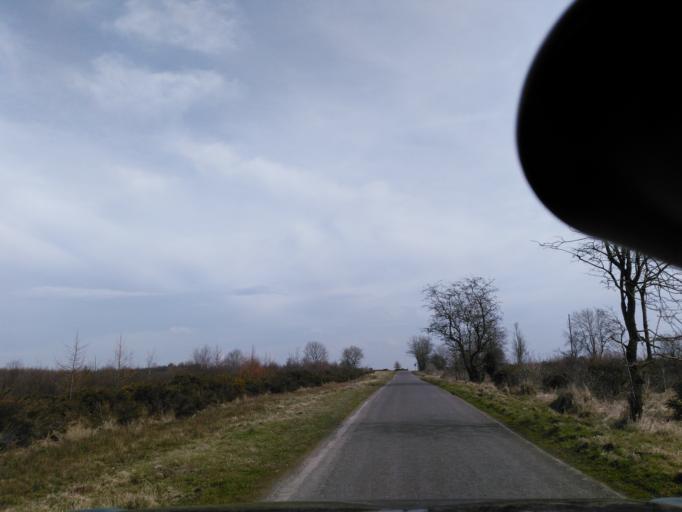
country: GB
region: England
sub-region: North Yorkshire
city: Angram Grange
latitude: 54.2318
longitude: -1.2039
